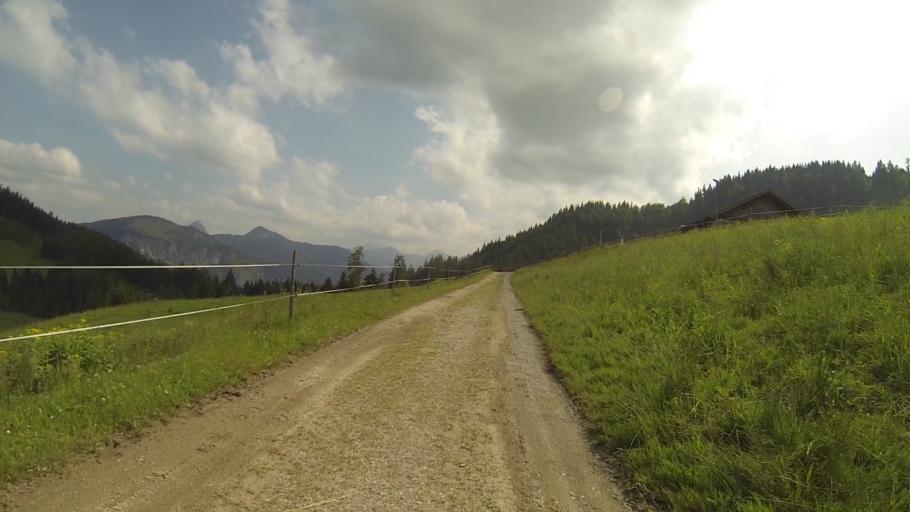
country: AT
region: Tyrol
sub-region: Politischer Bezirk Reutte
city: Jungholz
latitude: 47.5830
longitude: 10.4680
